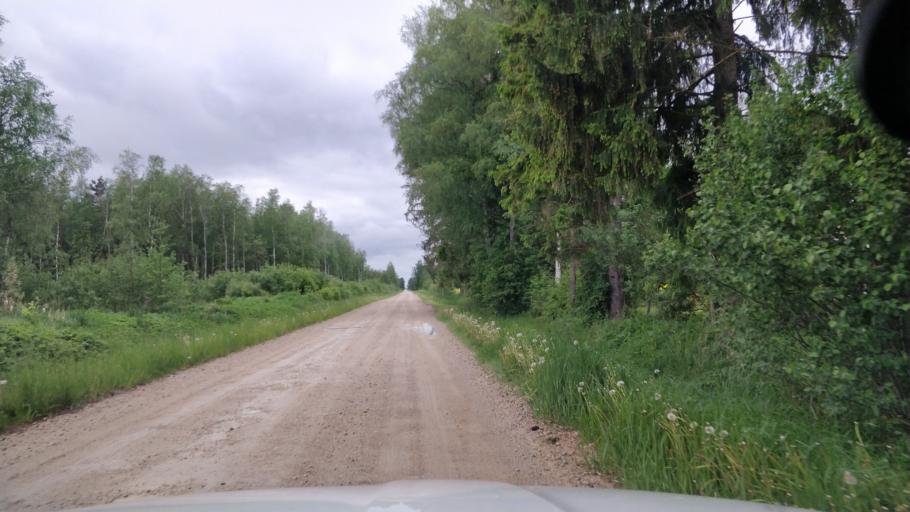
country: EE
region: Raplamaa
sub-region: Maerjamaa vald
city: Marjamaa
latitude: 58.7174
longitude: 24.2913
